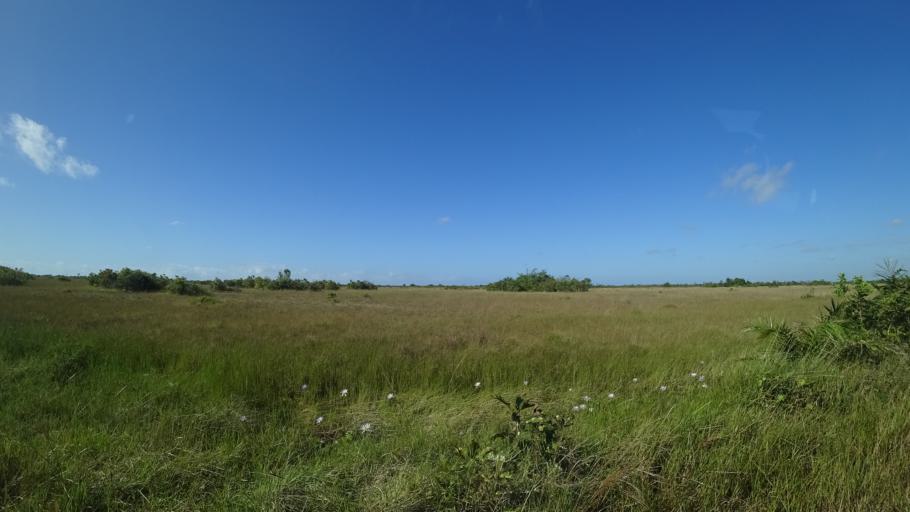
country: MZ
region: Sofala
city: Beira
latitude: -19.6959
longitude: 35.0338
